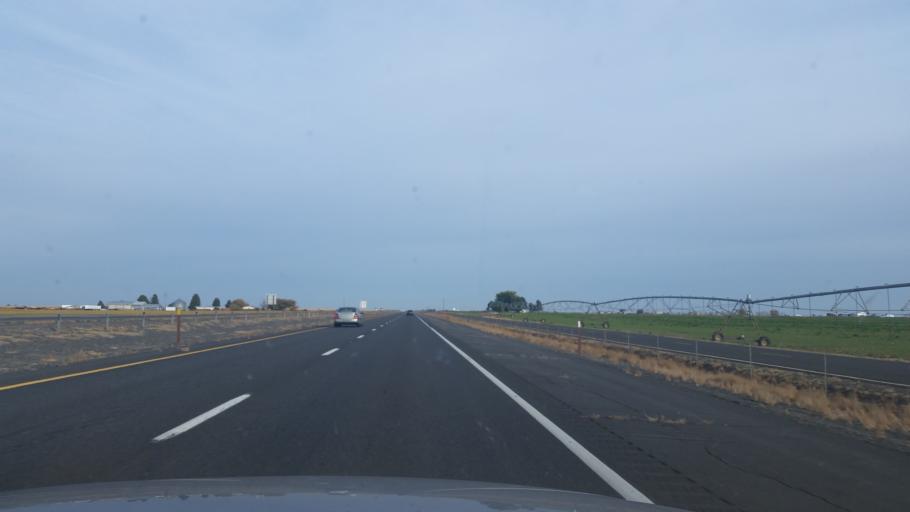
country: US
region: Washington
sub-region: Grant County
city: Quincy
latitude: 47.1033
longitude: -119.8095
